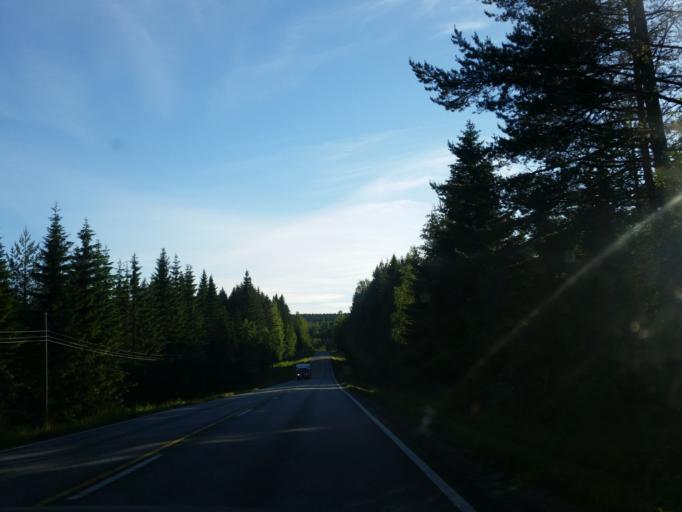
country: FI
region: Northern Savo
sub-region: Kuopio
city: Kuopio
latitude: 62.8453
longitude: 27.4396
